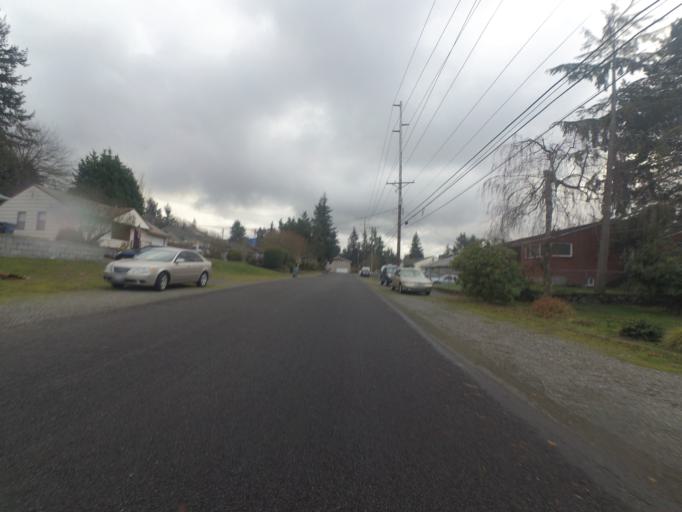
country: US
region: Washington
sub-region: Pierce County
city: University Place
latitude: 47.2292
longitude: -122.5391
